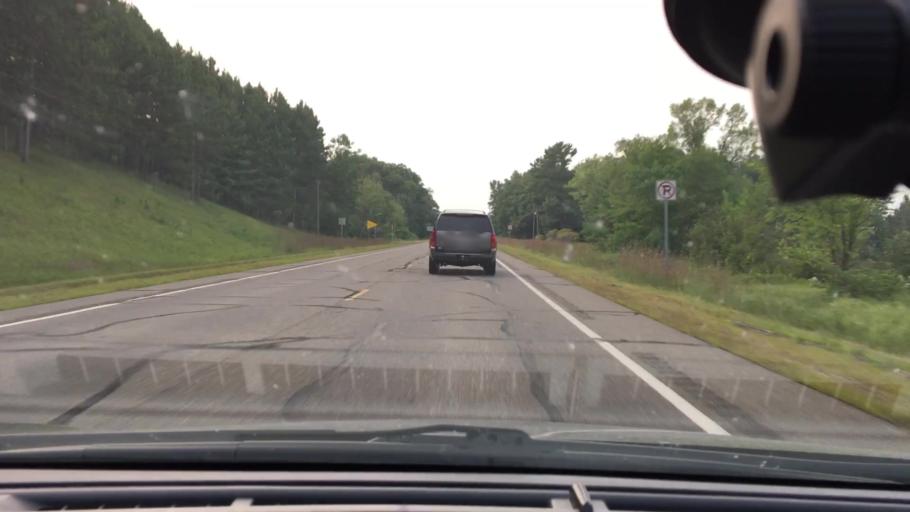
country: US
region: Minnesota
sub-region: Crow Wing County
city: Crosby
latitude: 46.3918
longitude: -93.8751
